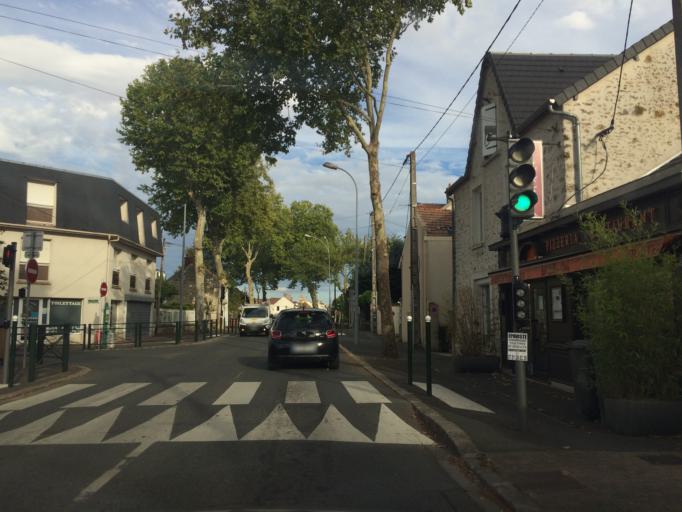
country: FR
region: Ile-de-France
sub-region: Departement de l'Essonne
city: Marolles-en-Hurepoix
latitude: 48.5630
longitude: 2.2966
